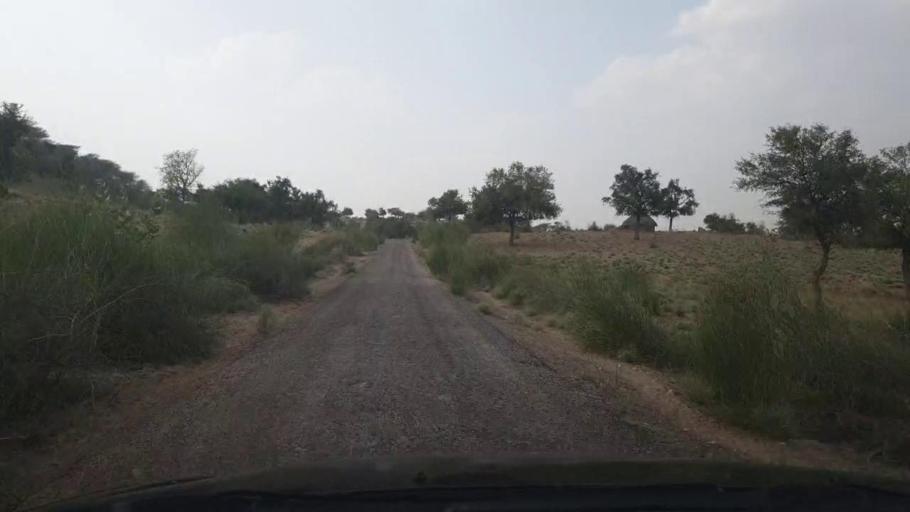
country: PK
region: Sindh
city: Islamkot
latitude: 24.9668
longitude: 70.6022
